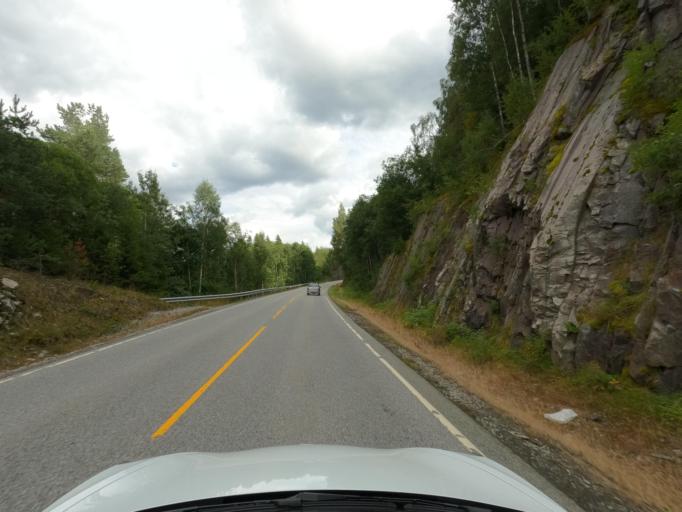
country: NO
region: Telemark
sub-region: Hjartdal
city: Sauland
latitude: 59.8330
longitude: 8.9695
